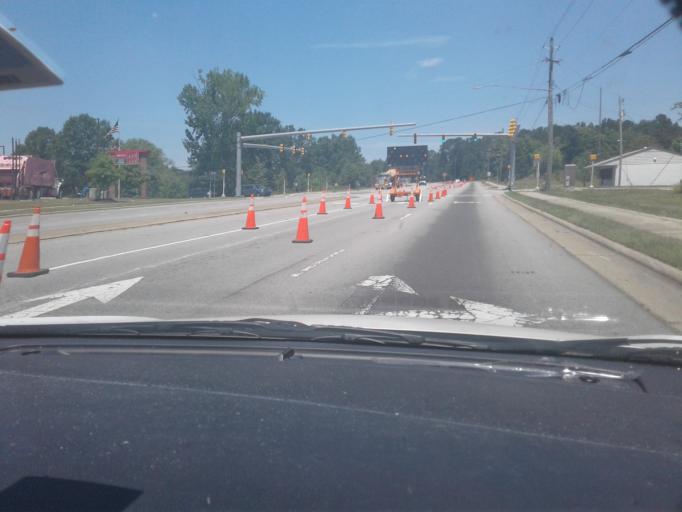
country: US
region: North Carolina
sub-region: Wake County
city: Fuquay-Varina
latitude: 35.6110
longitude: -78.8064
